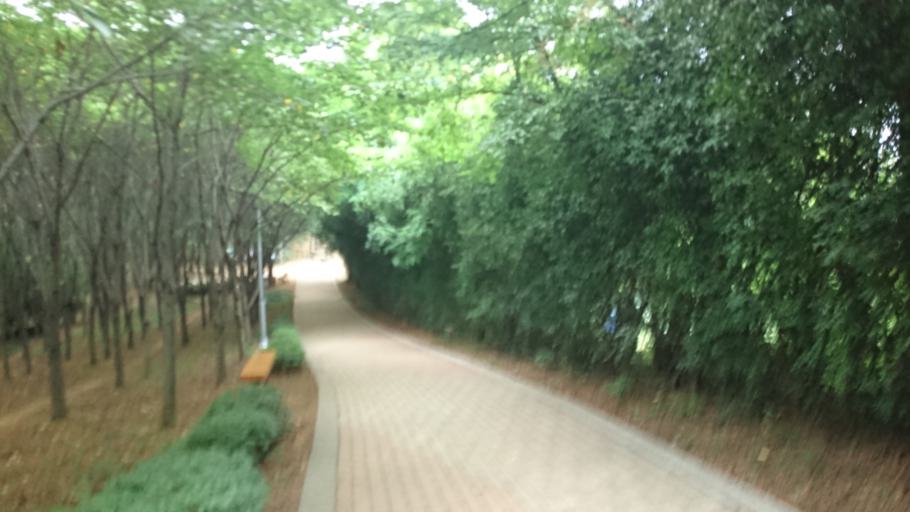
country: KR
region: Daegu
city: Daegu
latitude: 35.8623
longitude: 128.6331
